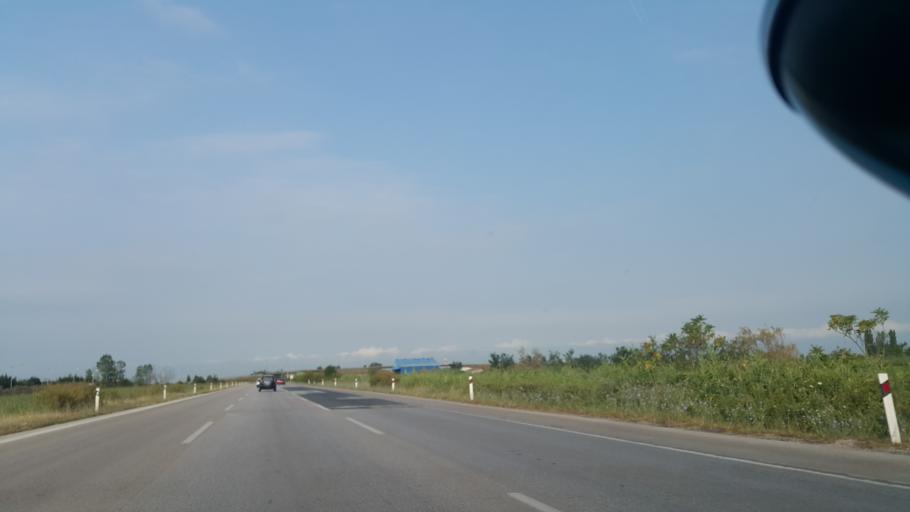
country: GR
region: Central Macedonia
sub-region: Nomos Thessalonikis
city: Chalastra
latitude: 40.6134
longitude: 22.7413
